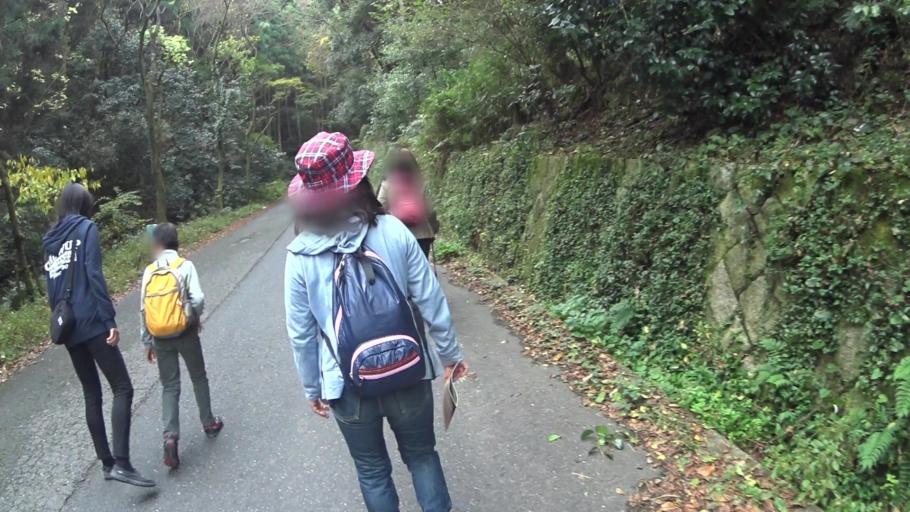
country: JP
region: Shiga Prefecture
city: Otsu-shi
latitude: 35.0059
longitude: 135.8505
